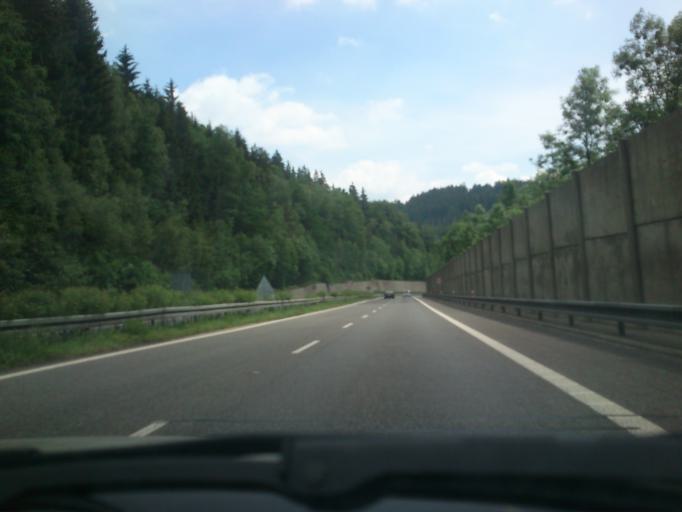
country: CZ
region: Liberecky
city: Hodkovice nad Mohelkou
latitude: 50.6926
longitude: 15.1061
